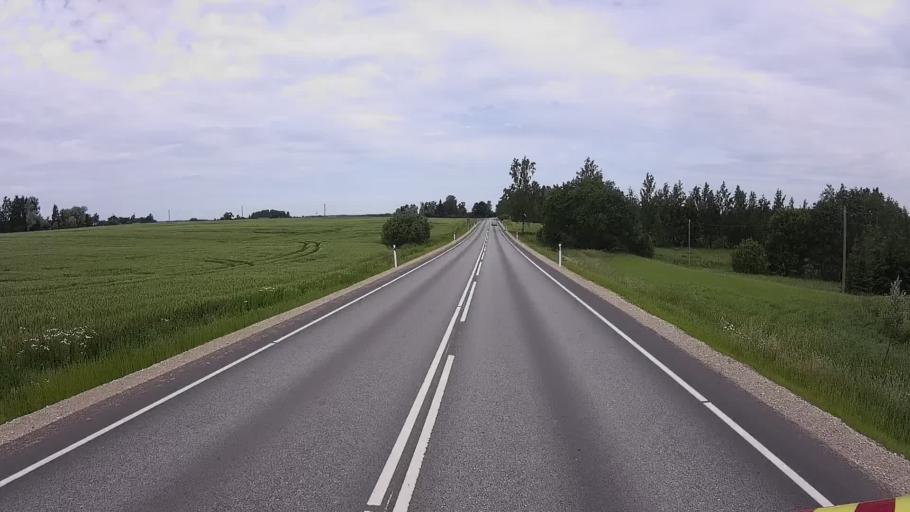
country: EE
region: Viljandimaa
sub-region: Viljandi linn
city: Viljandi
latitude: 58.2659
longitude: 25.5855
